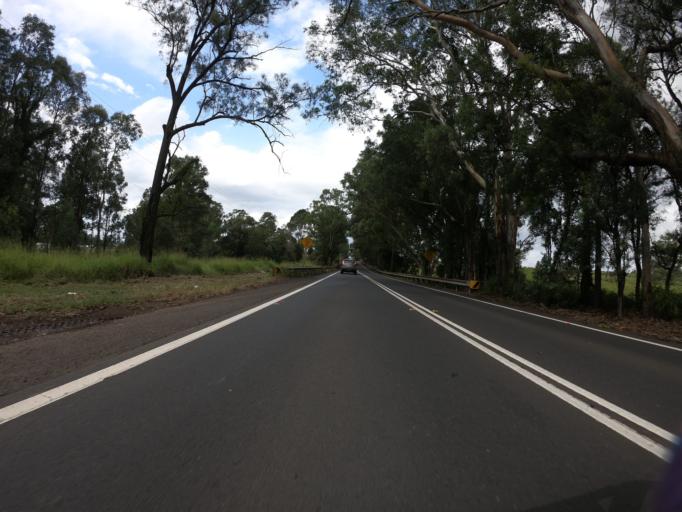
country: AU
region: New South Wales
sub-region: Blacktown
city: Riverstone
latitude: -33.6651
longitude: 150.8885
